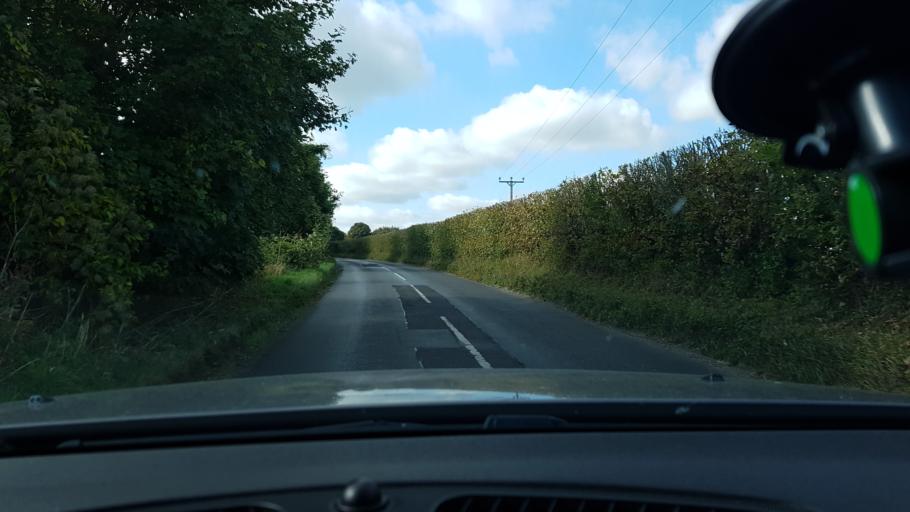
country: GB
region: England
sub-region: West Berkshire
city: Kintbury
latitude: 51.4034
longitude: -1.4708
